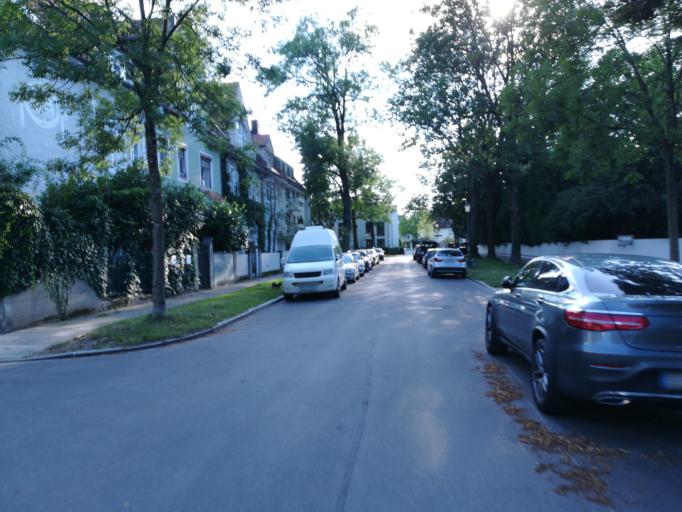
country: DE
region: Bavaria
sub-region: Upper Bavaria
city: Munich
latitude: 48.1603
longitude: 11.5234
